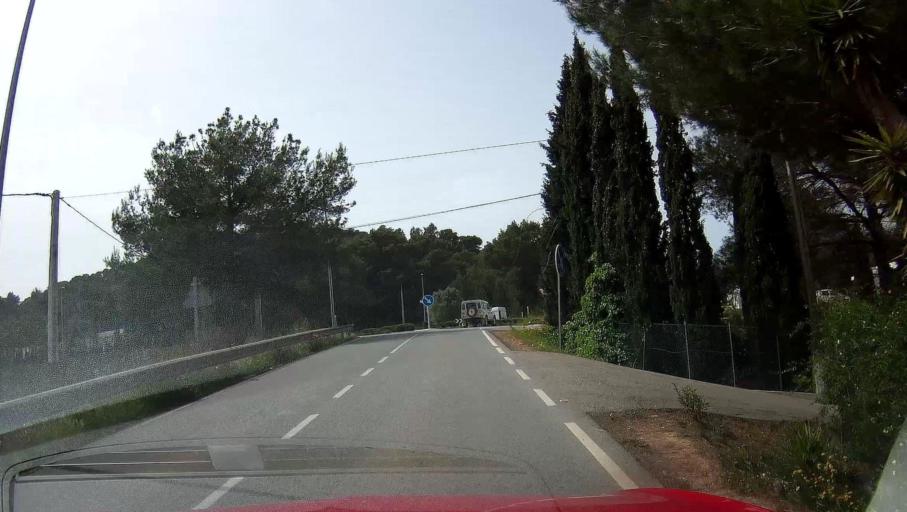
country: ES
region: Balearic Islands
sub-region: Illes Balears
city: Santa Eularia des Riu
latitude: 38.9908
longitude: 1.4857
